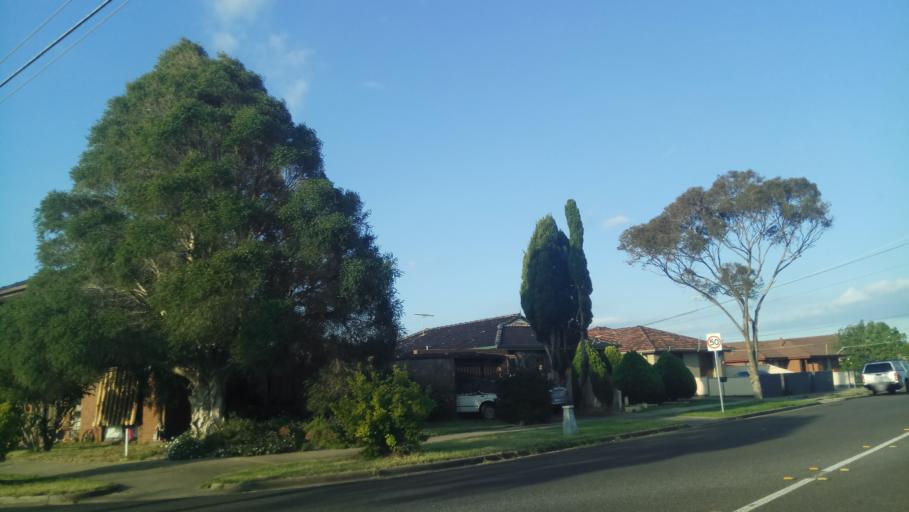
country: AU
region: Victoria
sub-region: Hobsons Bay
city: Altona Meadows
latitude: -37.8856
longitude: 144.7859
